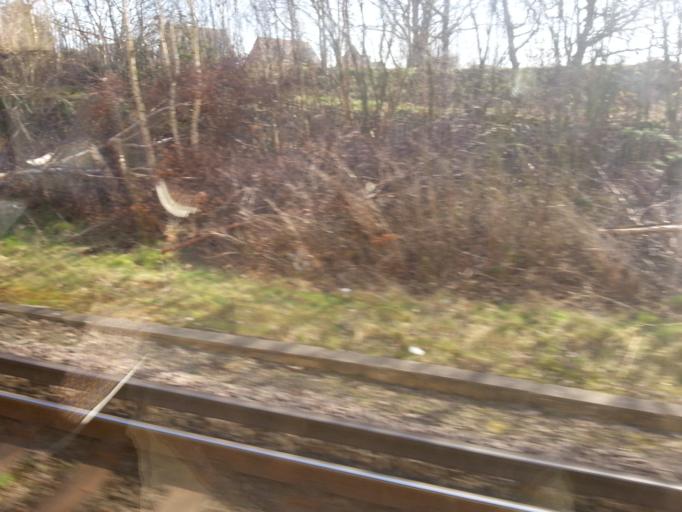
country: GB
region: England
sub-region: Metropolitan Borough of Wirral
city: Bromborough
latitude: 53.3576
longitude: -2.9085
